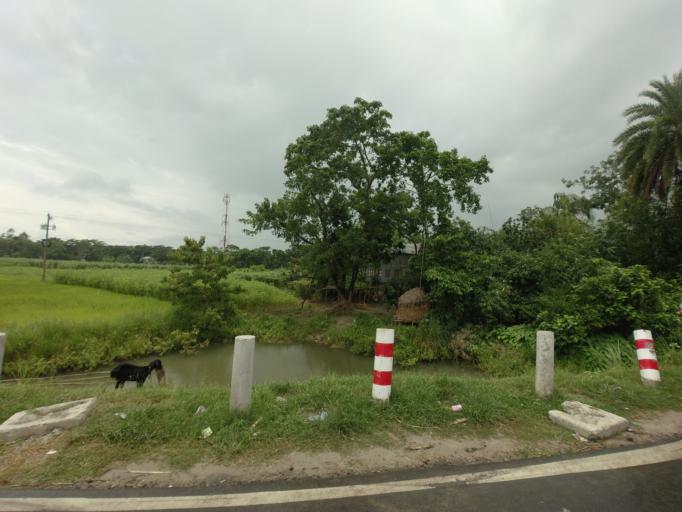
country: BD
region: Dhaka
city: Char Bhadrasan
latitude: 23.4113
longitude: 90.2152
